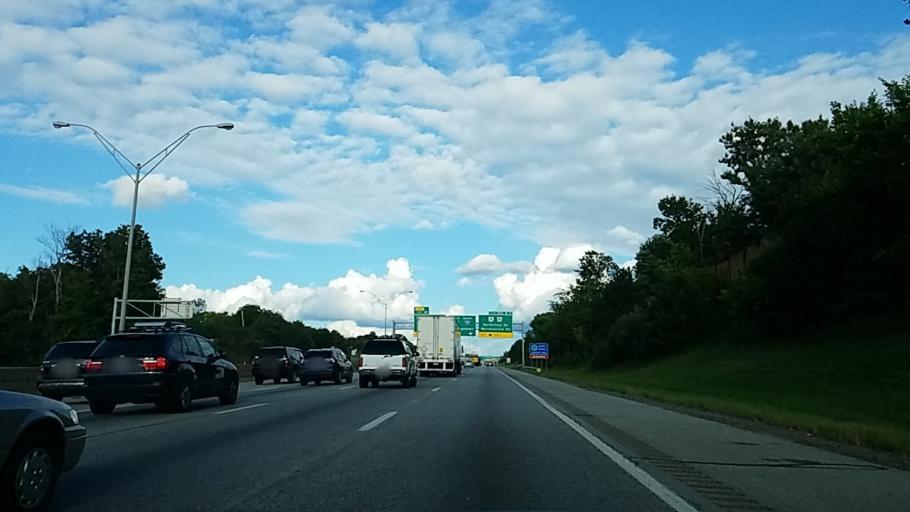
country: US
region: Ohio
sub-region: Cuyahoga County
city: Maple Heights
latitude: 41.4247
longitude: -81.5537
